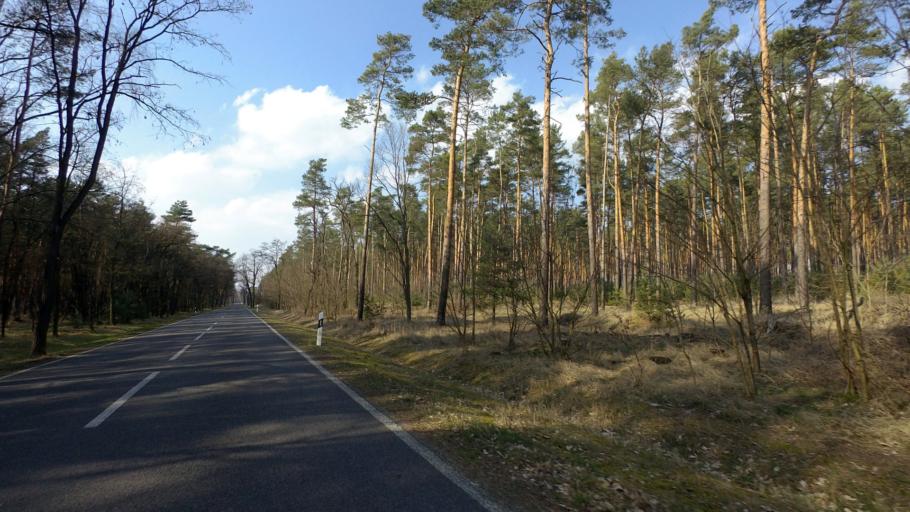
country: DE
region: Brandenburg
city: Dahme
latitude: 51.9188
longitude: 13.4815
